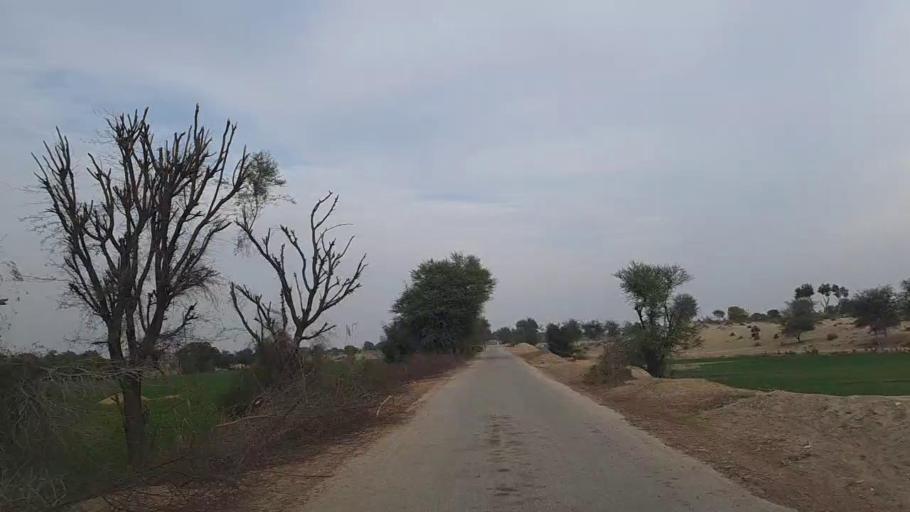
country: PK
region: Sindh
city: Daur
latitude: 26.5149
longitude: 68.4756
